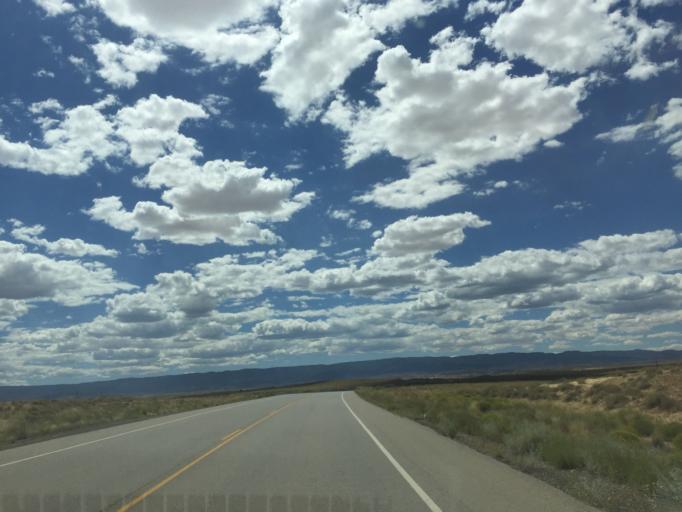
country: US
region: New Mexico
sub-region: San Juan County
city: Shiprock
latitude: 36.3370
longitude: -108.7038
